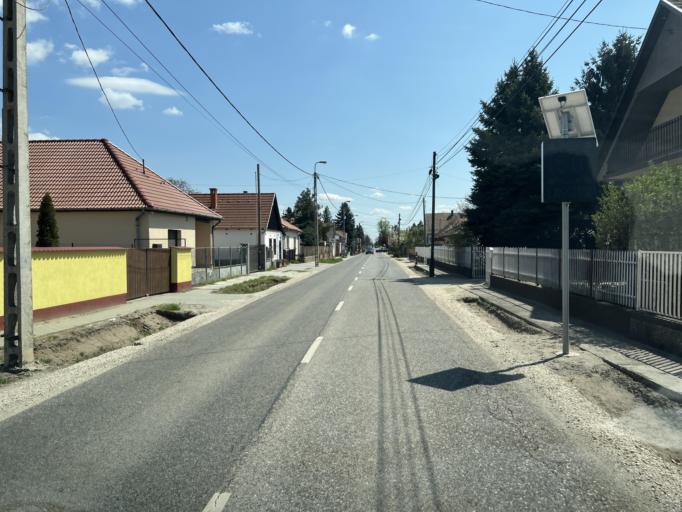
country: HU
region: Pest
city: Inarcs
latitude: 47.2629
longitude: 19.3278
